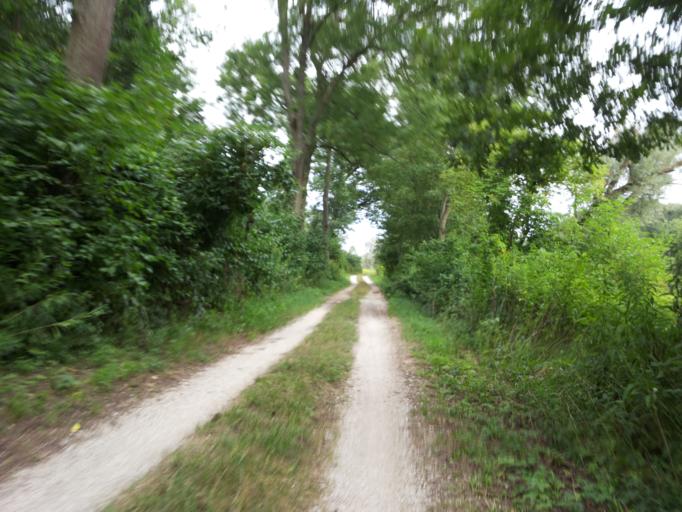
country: DE
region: Bavaria
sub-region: Upper Bavaria
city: Weichering
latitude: 48.7430
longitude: 11.3016
